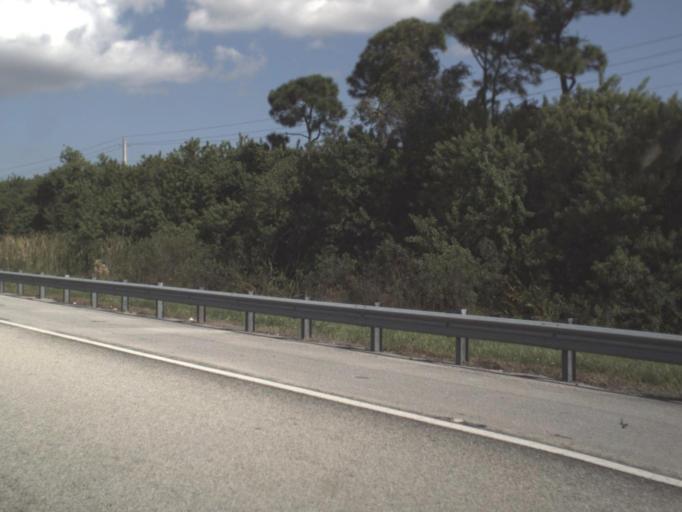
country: US
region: Florida
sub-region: Palm Beach County
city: Palm Beach Gardens
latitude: 26.8334
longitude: -80.1302
